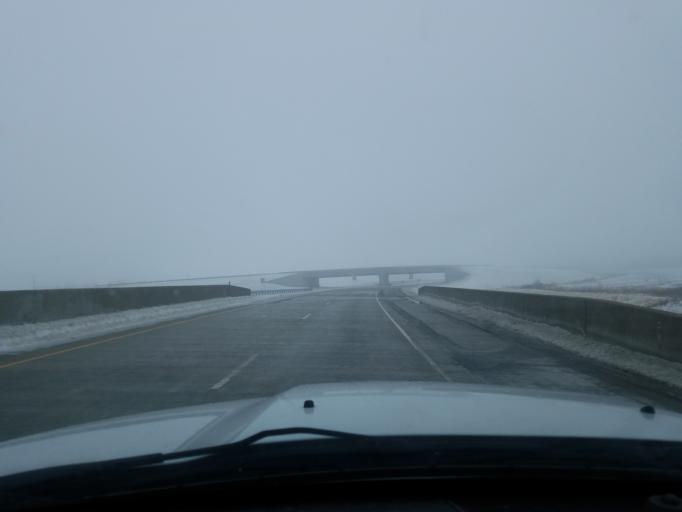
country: US
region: Indiana
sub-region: Howard County
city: Kokomo
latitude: 40.5400
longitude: -86.1242
